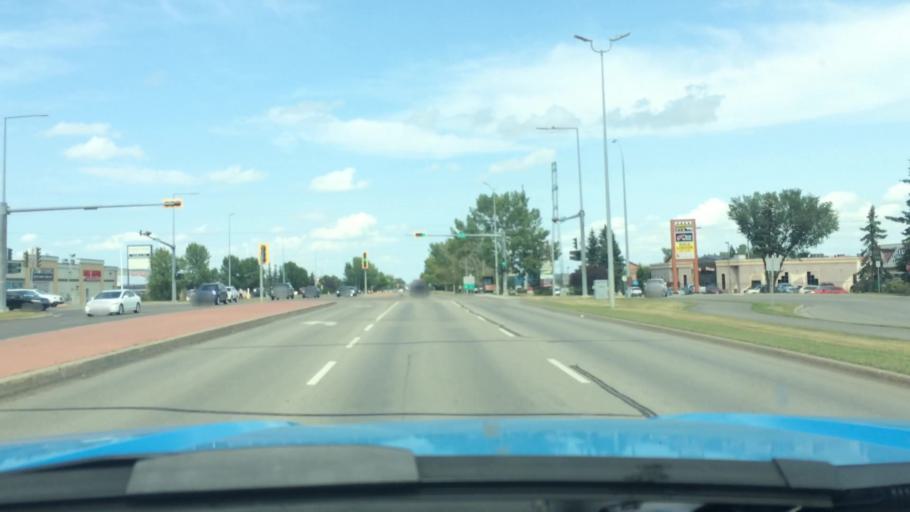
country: CA
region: Alberta
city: Red Deer
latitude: 52.2347
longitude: -113.8139
